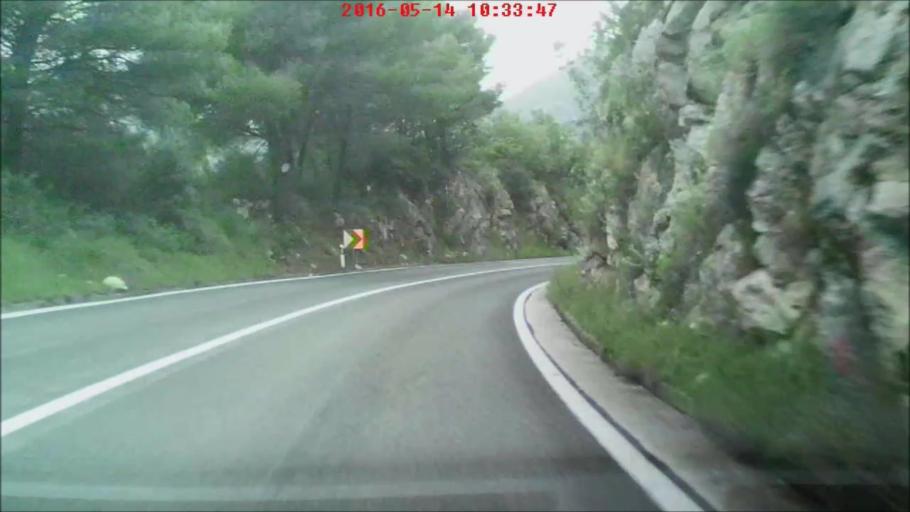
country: HR
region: Dubrovacko-Neretvanska
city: Podgora
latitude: 42.7767
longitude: 17.8873
